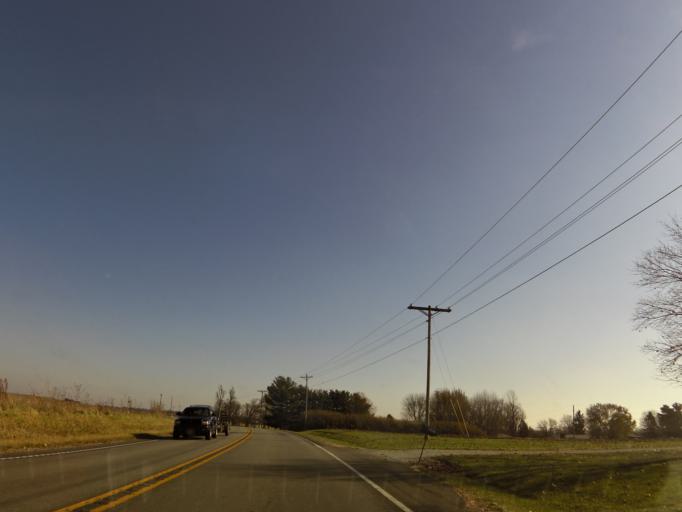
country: US
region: Indiana
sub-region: Fayette County
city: Connersville
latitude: 39.6355
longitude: -85.0565
